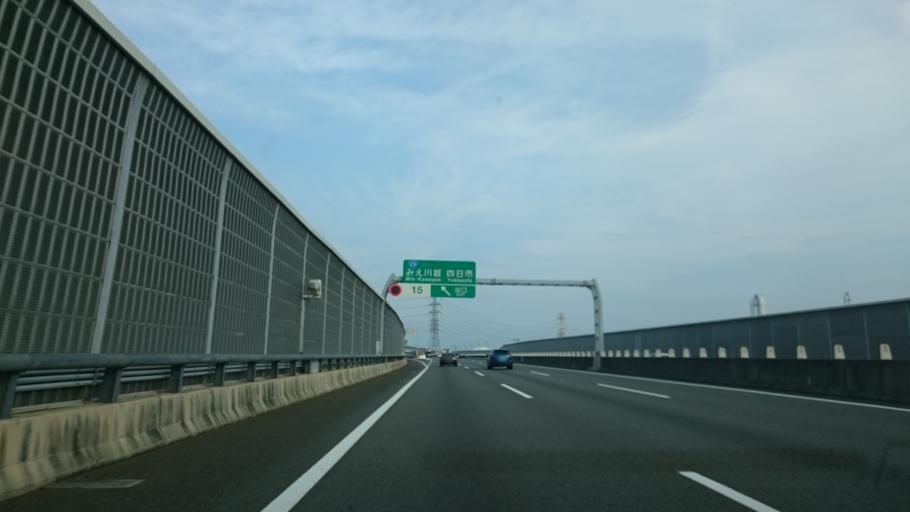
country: JP
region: Mie
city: Yokkaichi
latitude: 35.0240
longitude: 136.6809
